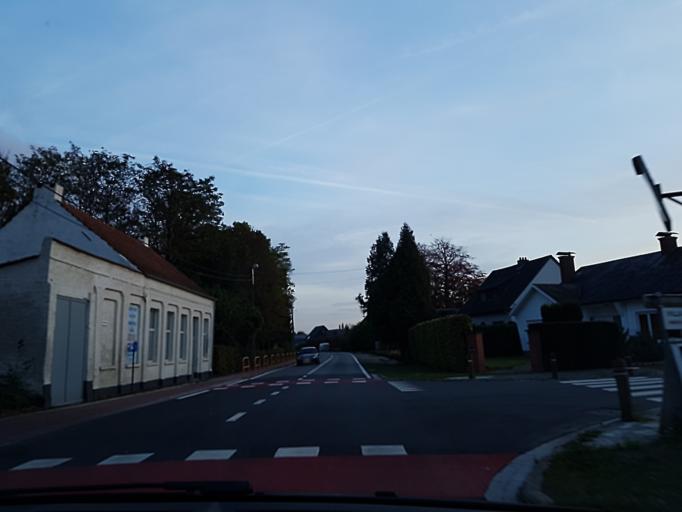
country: BE
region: Flanders
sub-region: Provincie Antwerpen
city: Lier
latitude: 51.1558
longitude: 4.5767
